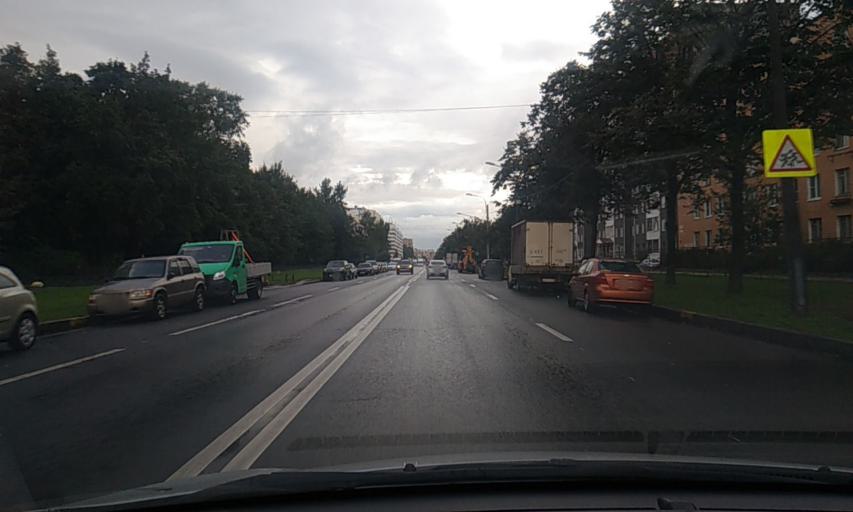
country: RU
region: St.-Petersburg
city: Dachnoye
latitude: 59.8261
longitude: 30.2233
